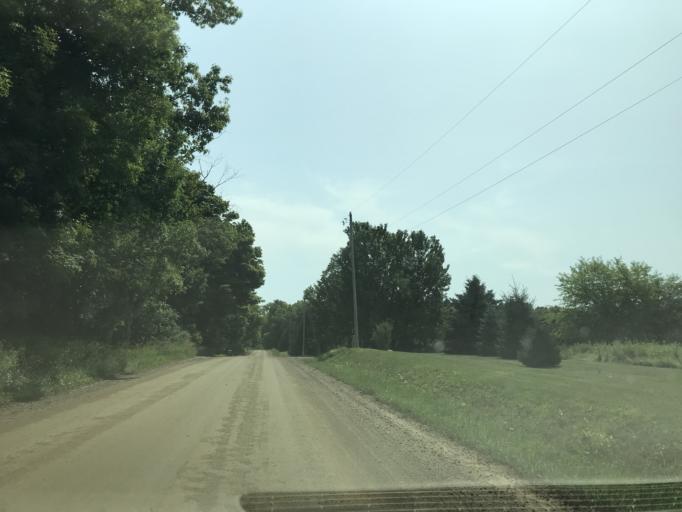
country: US
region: Michigan
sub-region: Eaton County
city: Grand Ledge
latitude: 42.7699
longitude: -84.6941
